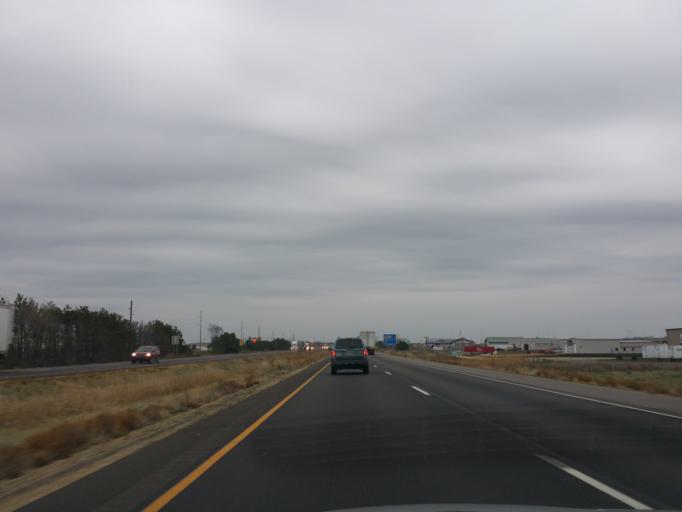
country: US
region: Wisconsin
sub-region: Dunn County
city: Menomonie
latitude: 44.9048
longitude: -91.8689
